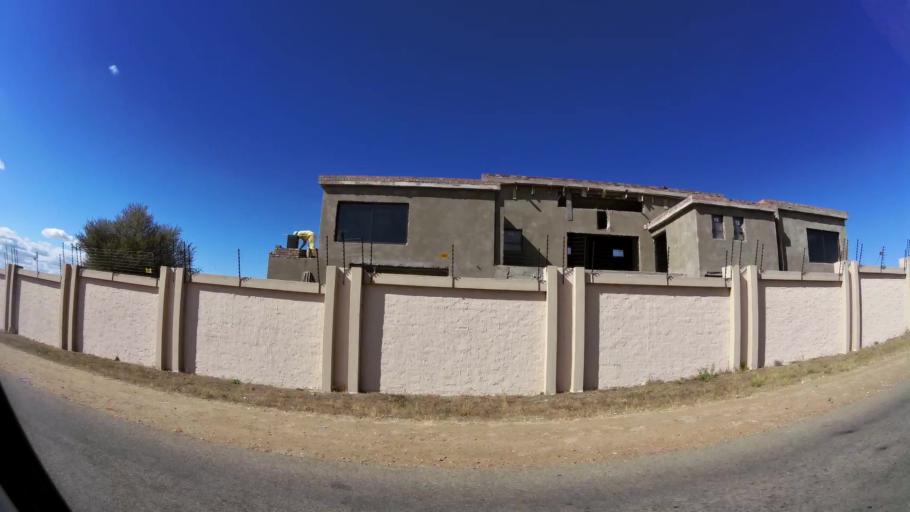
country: ZA
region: Limpopo
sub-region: Capricorn District Municipality
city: Polokwane
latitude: -23.8677
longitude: 29.5095
